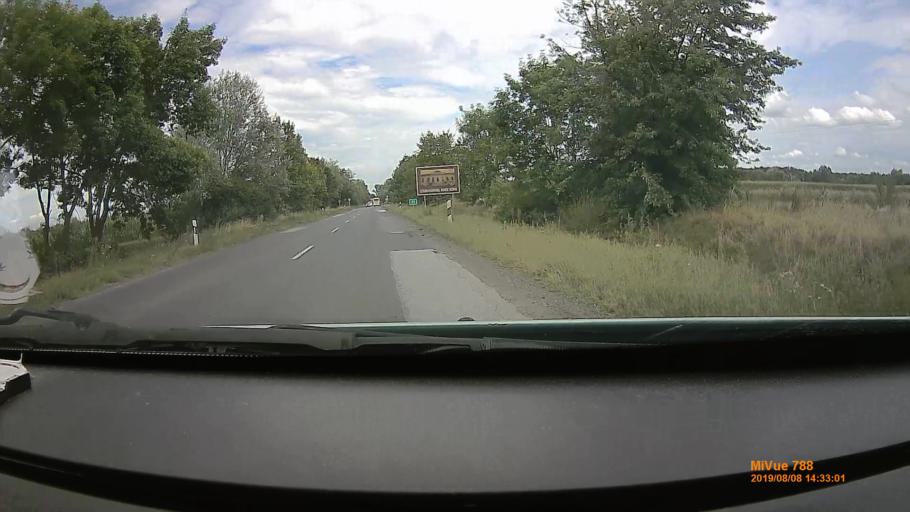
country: HU
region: Szabolcs-Szatmar-Bereg
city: Mateszalka
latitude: 47.9406
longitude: 22.3472
